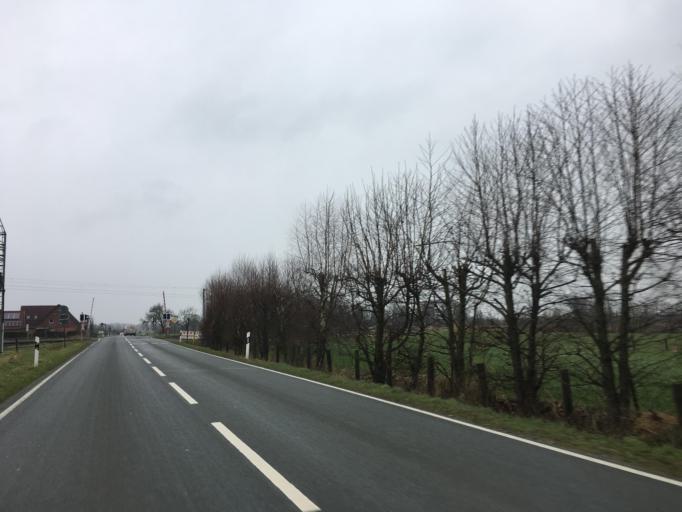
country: DE
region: North Rhine-Westphalia
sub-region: Regierungsbezirk Munster
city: Dulmen
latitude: 51.8548
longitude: 7.3493
